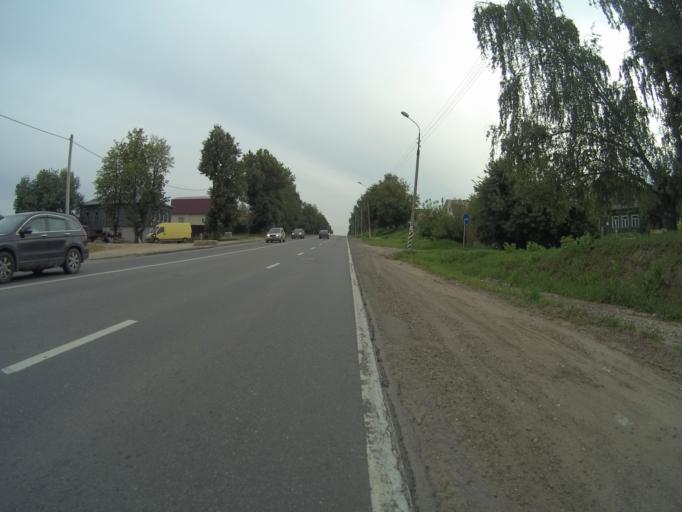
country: RU
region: Vladimir
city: Bogolyubovo
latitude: 56.1904
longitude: 40.5244
